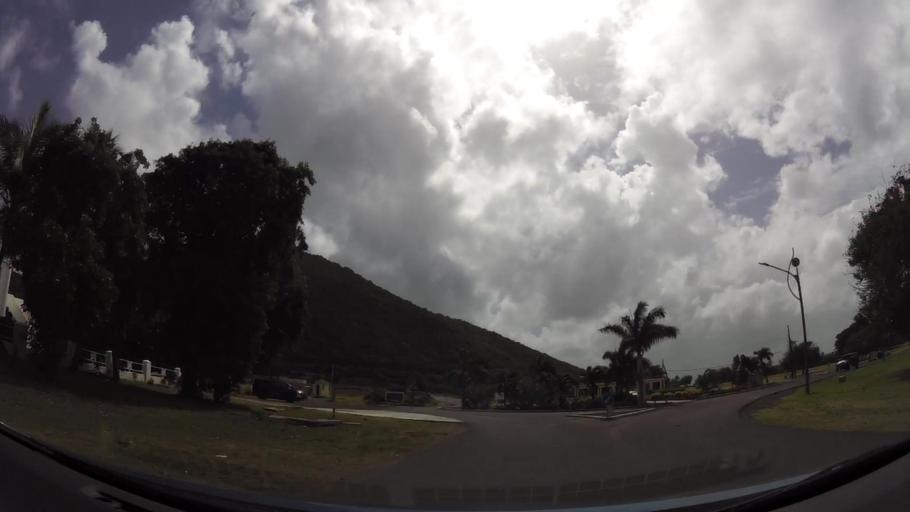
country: KN
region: Saint George Basseterre
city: Basseterre
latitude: 17.2841
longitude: -62.6850
